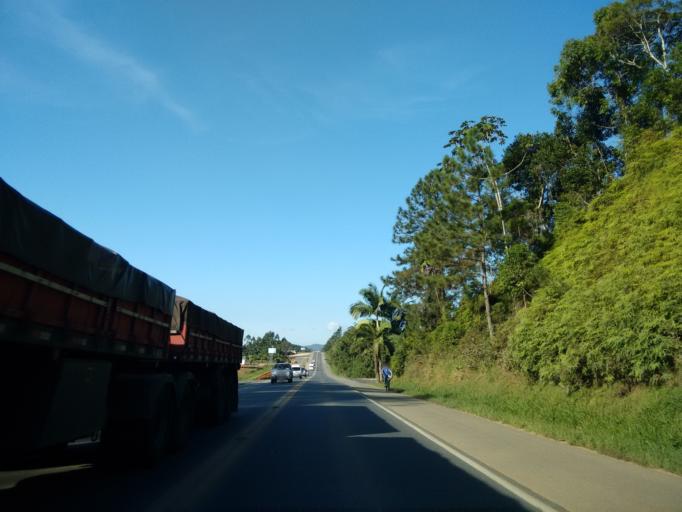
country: BR
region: Santa Catarina
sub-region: Guaramirim
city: Guaramirim
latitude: -26.4536
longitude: -48.9180
